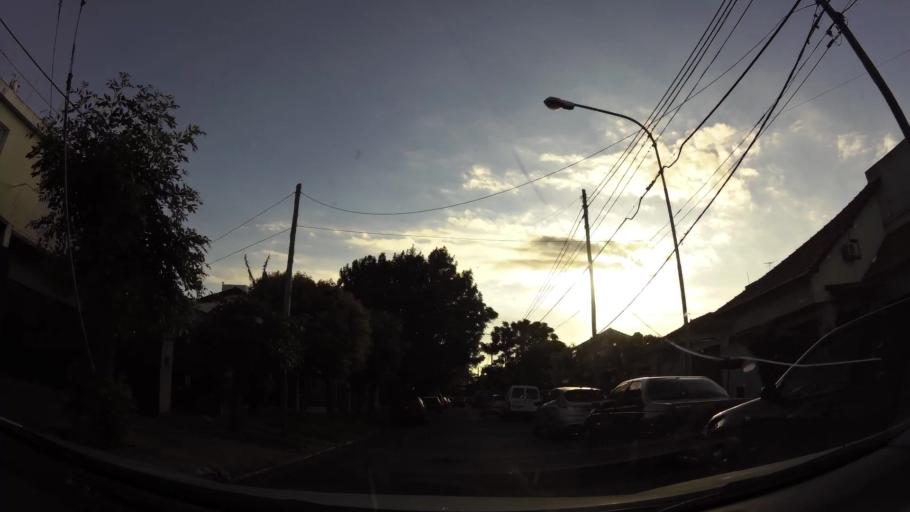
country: AR
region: Buenos Aires
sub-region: Partido de Tigre
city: Tigre
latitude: -34.4566
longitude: -58.6302
